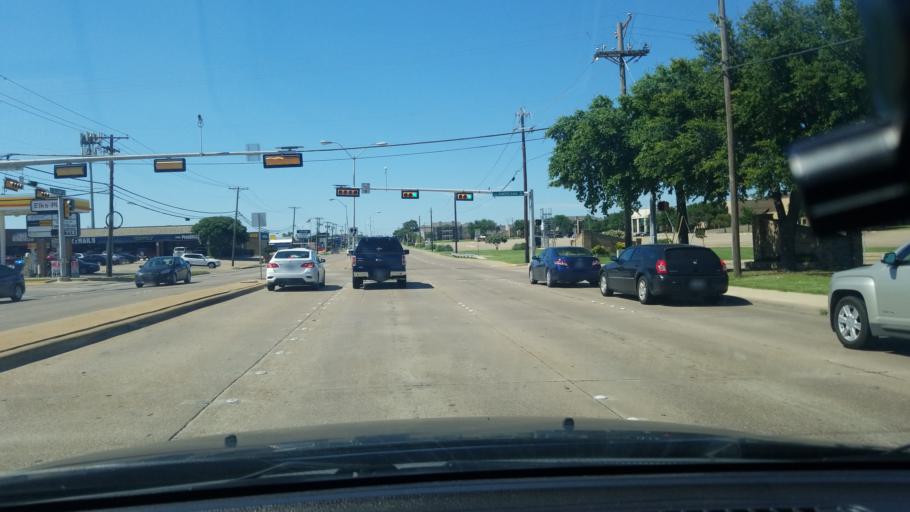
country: US
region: Texas
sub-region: Dallas County
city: Mesquite
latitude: 32.8047
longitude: -96.6112
